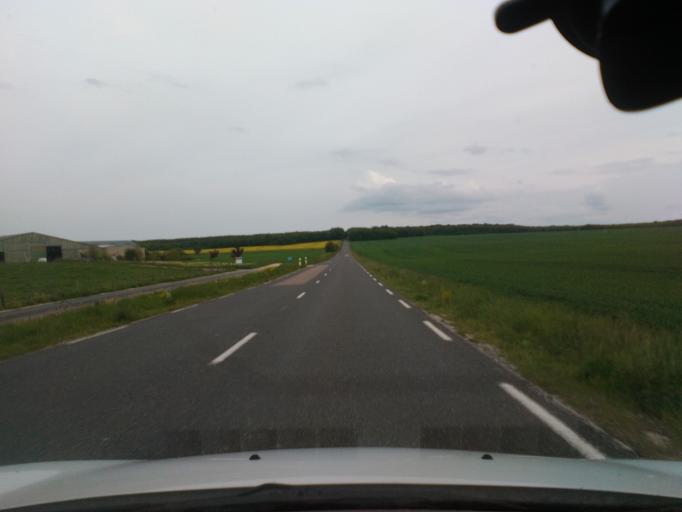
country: FR
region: Champagne-Ardenne
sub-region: Departement de la Haute-Marne
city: Lavilleneuve-au-Roi
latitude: 48.2214
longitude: 4.8966
